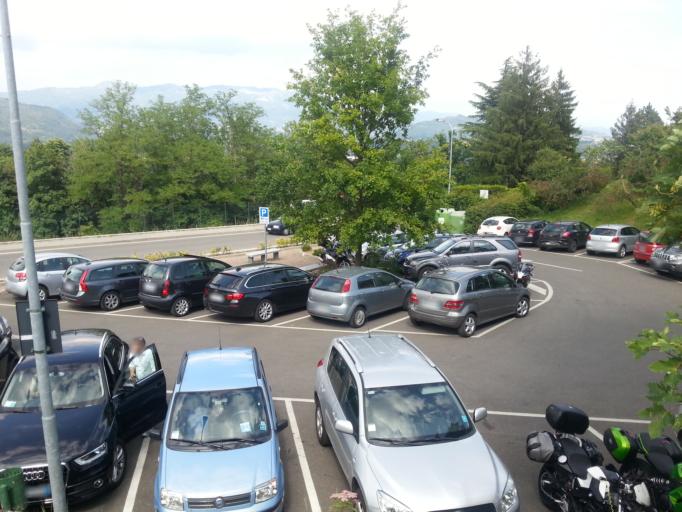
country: IT
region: Lombardy
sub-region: Provincia di Lecco
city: Montevecchia
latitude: 45.7072
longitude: 9.3728
